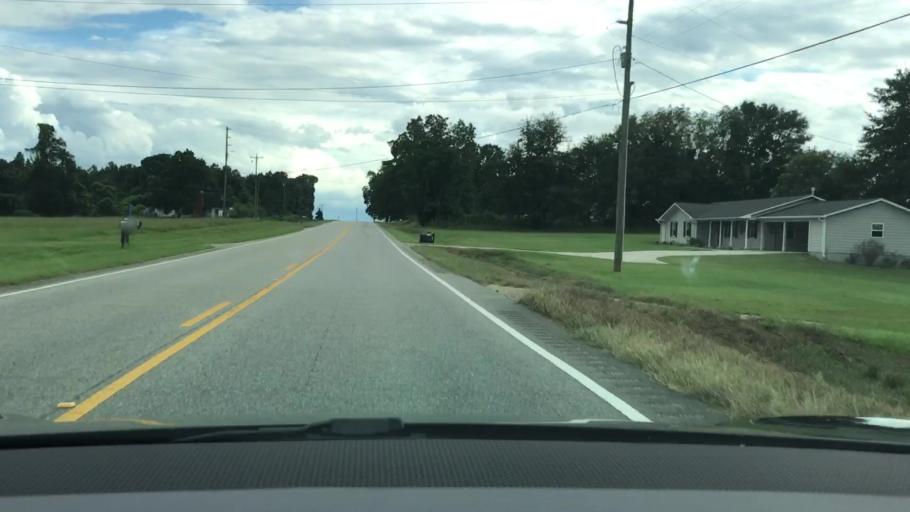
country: US
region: Alabama
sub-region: Pike County
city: Troy
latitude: 31.6667
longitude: -85.9592
